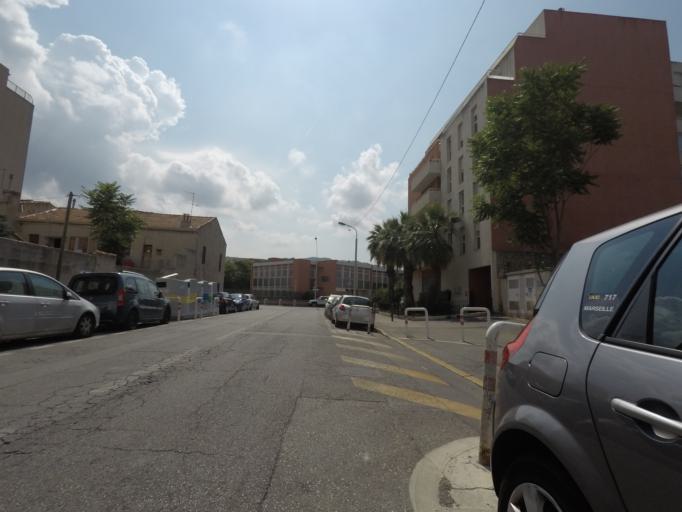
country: FR
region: Provence-Alpes-Cote d'Azur
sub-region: Departement des Bouches-du-Rhone
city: Marseille 10
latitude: 43.2790
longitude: 5.4095
